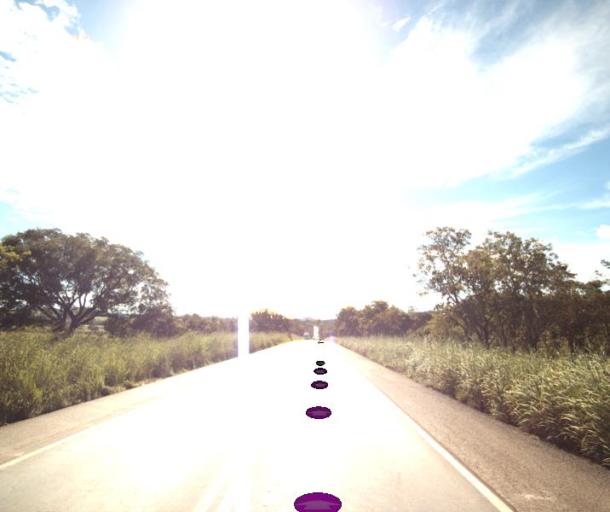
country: BR
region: Goias
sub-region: Uruana
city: Uruana
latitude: -15.5347
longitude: -49.4465
